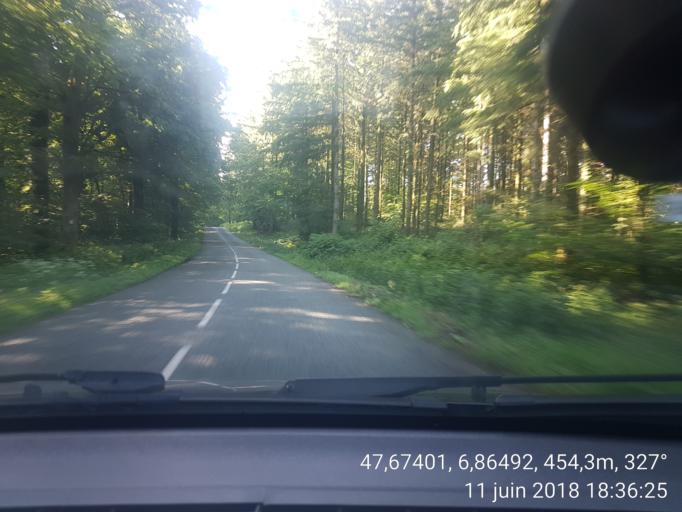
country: FR
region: Franche-Comte
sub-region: Territoire de Belfort
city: Offemont
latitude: 47.6739
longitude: 6.8650
